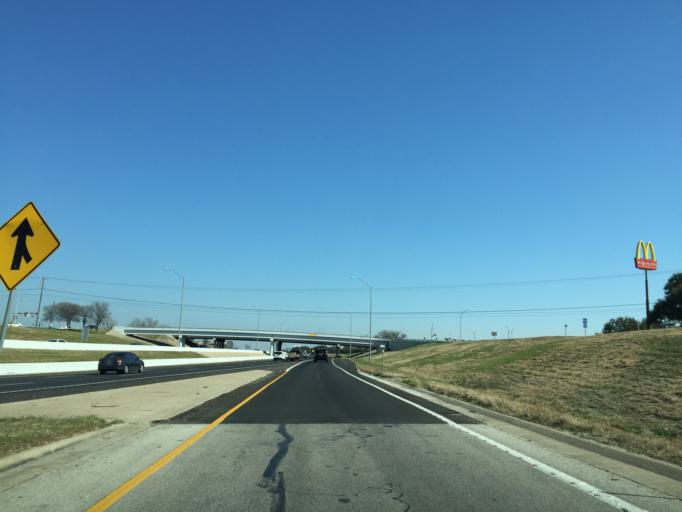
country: US
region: Texas
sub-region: Williamson County
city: Georgetown
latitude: 30.6480
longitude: -97.6807
